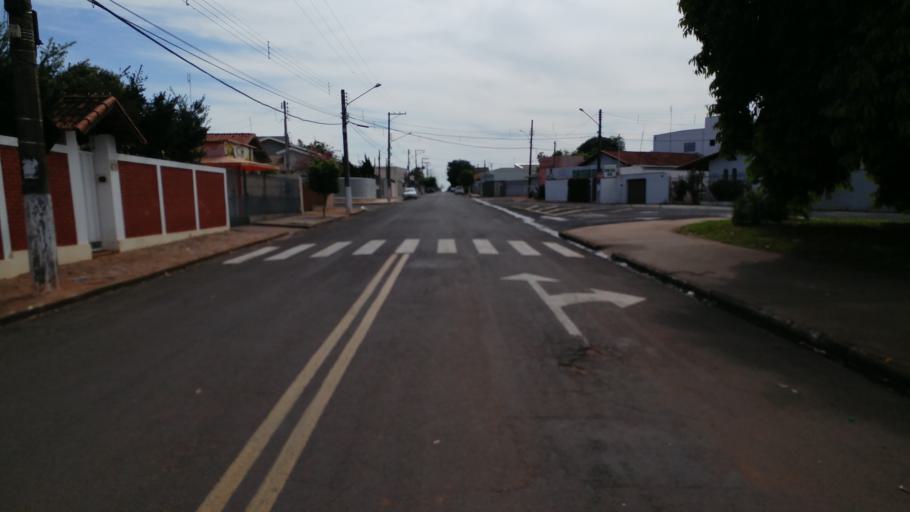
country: BR
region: Sao Paulo
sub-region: Paraguacu Paulista
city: Paraguacu Paulista
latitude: -22.4075
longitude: -50.5794
